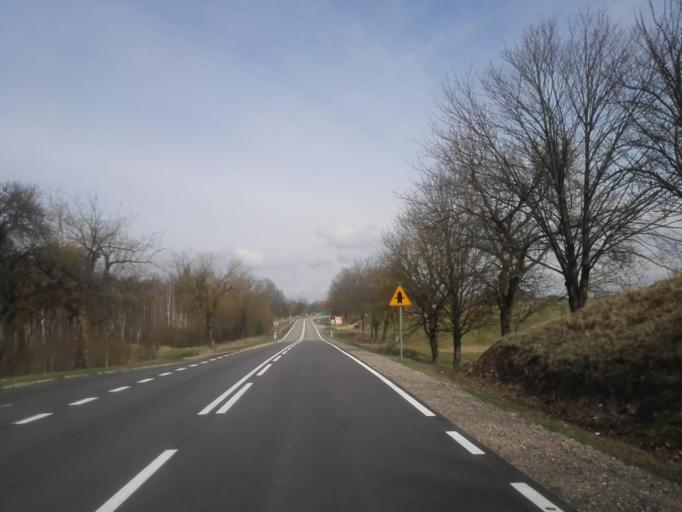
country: PL
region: Podlasie
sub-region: Powiat sejnenski
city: Sejny
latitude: 54.0613
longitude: 23.3575
